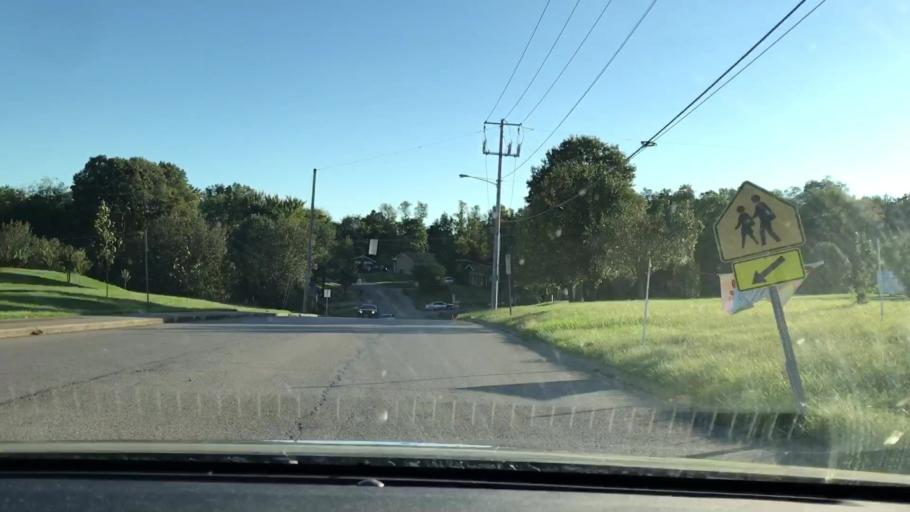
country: US
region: Tennessee
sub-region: Williamson County
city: Brentwood Estates
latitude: 36.0579
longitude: -86.6994
